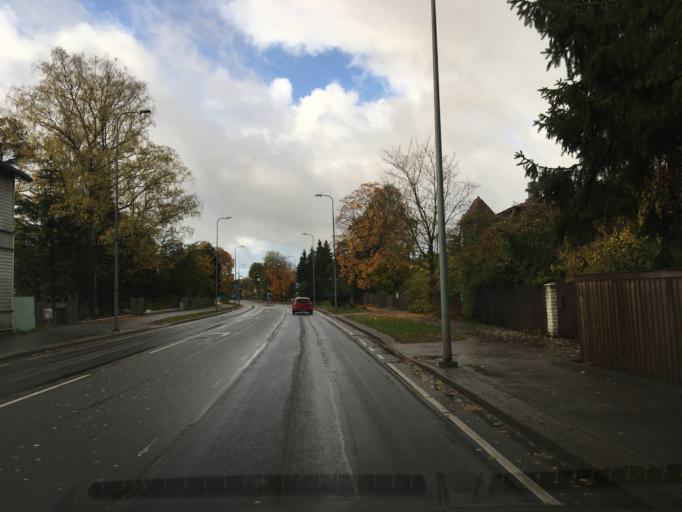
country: EE
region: Harju
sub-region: Saue vald
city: Laagri
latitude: 59.3782
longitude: 24.6539
